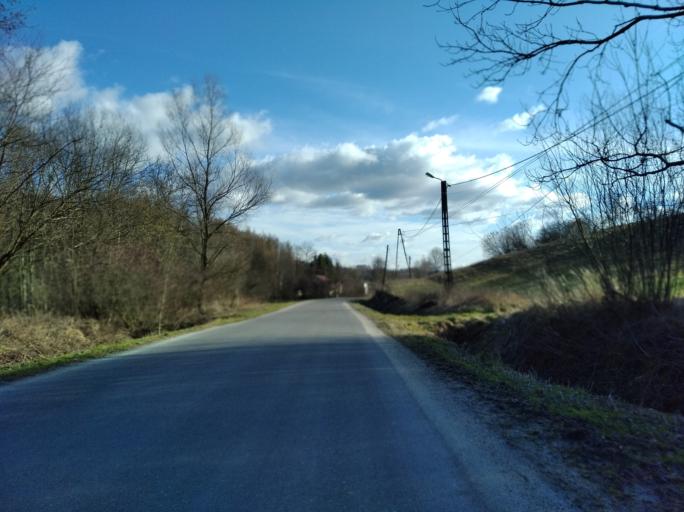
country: PL
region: Subcarpathian Voivodeship
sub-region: Powiat strzyzowski
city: Wisniowa
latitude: 49.8925
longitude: 21.7119
